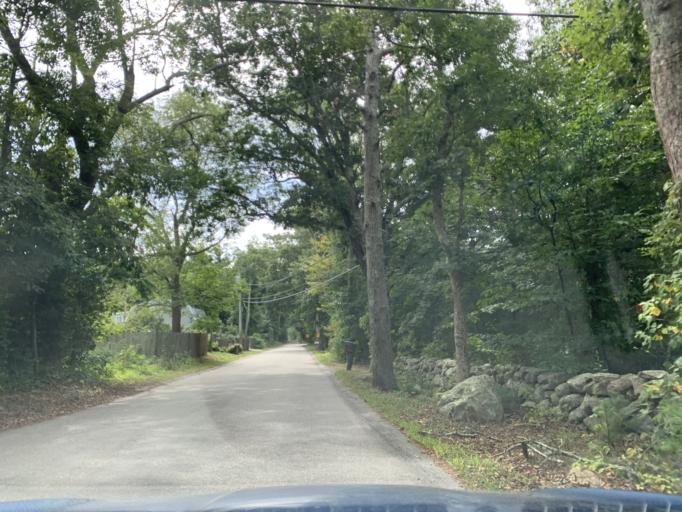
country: US
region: Rhode Island
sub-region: Washington County
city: Exeter
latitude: 41.5399
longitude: -71.6160
